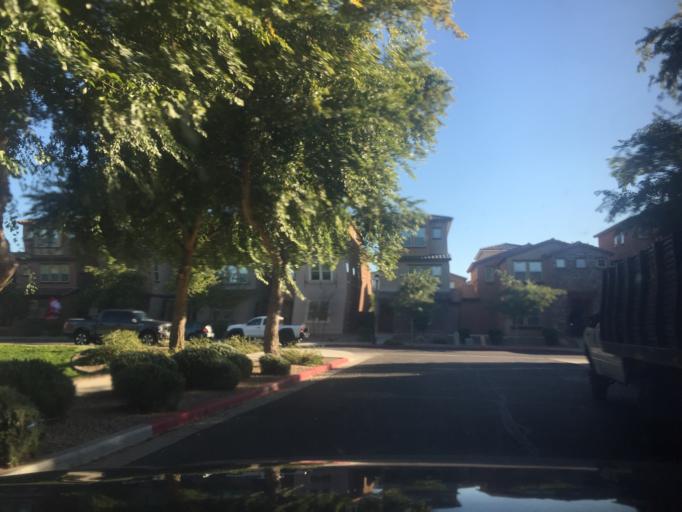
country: US
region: Arizona
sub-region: Maricopa County
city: Tolleson
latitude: 33.4706
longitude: -112.2268
